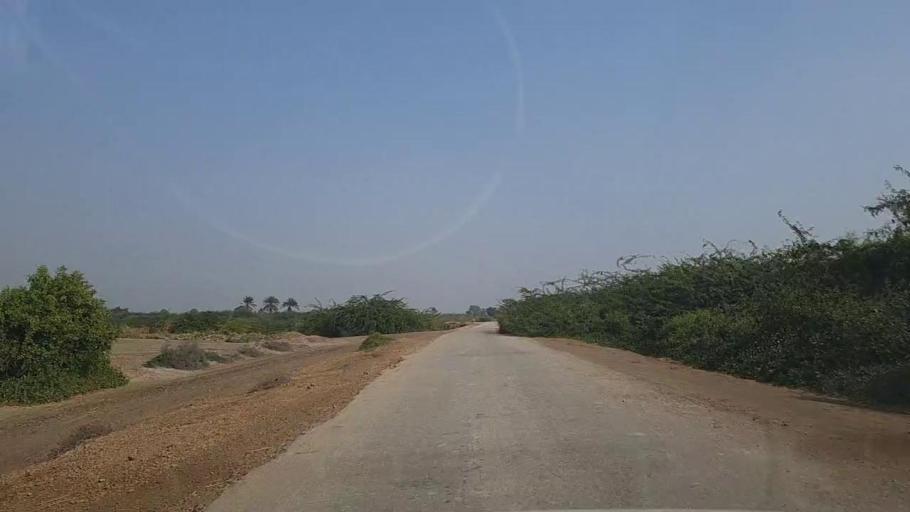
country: PK
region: Sindh
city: Keti Bandar
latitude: 24.2433
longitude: 67.7026
